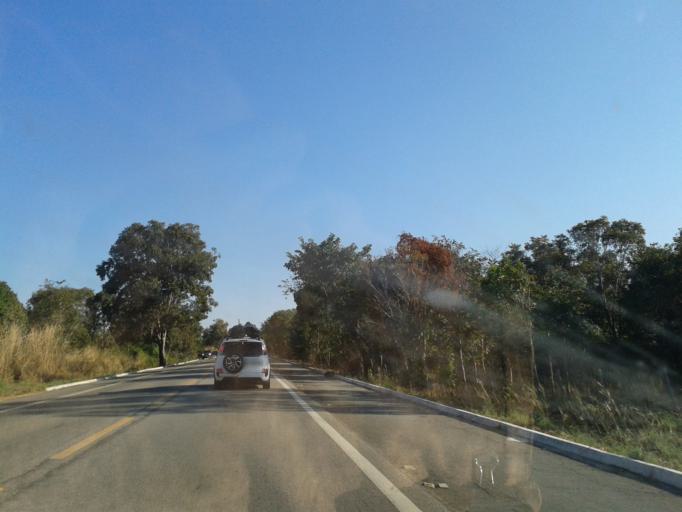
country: BR
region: Goias
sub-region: Mozarlandia
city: Mozarlandia
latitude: -15.2835
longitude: -50.4738
